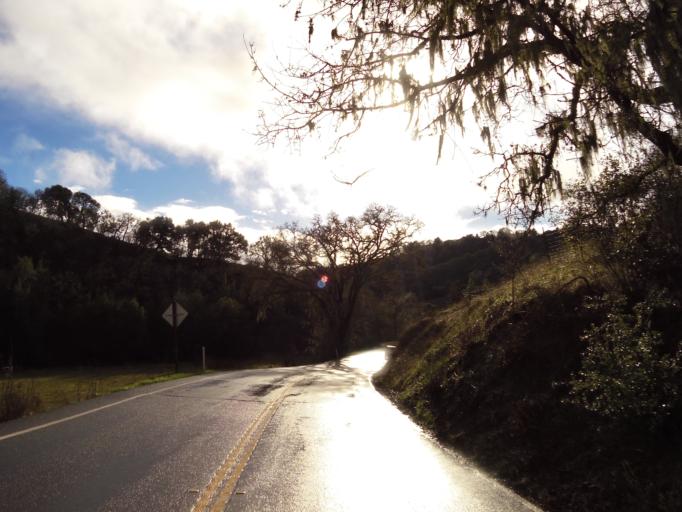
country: US
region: California
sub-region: Sonoma County
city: Cloverdale
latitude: 38.8825
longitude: -123.1353
